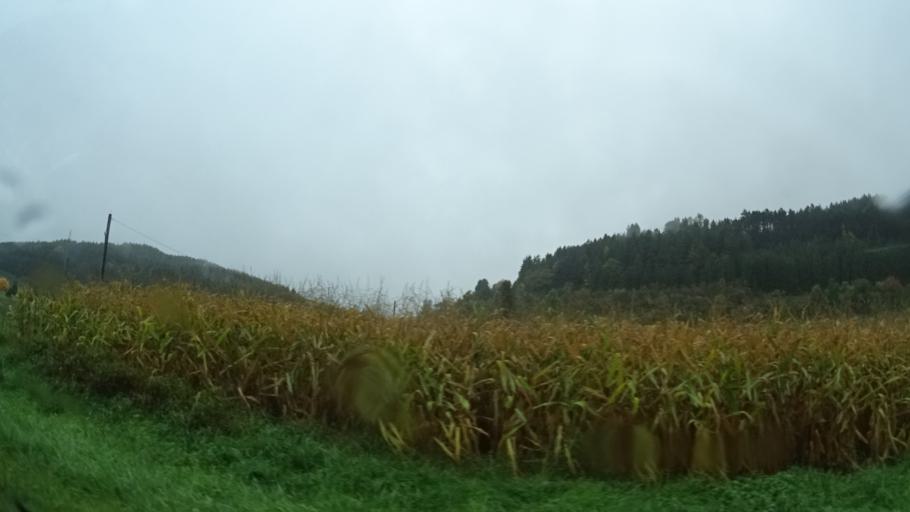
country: DE
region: Bavaria
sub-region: Upper Franconia
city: Marktrodach
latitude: 50.2695
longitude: 11.3573
